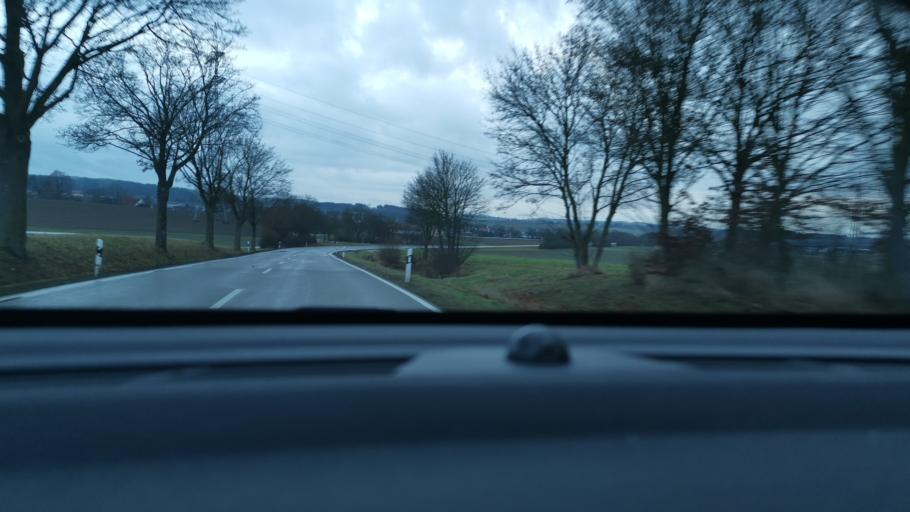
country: DE
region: Bavaria
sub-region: Swabia
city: Petersdorf
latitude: 48.5169
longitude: 11.0252
